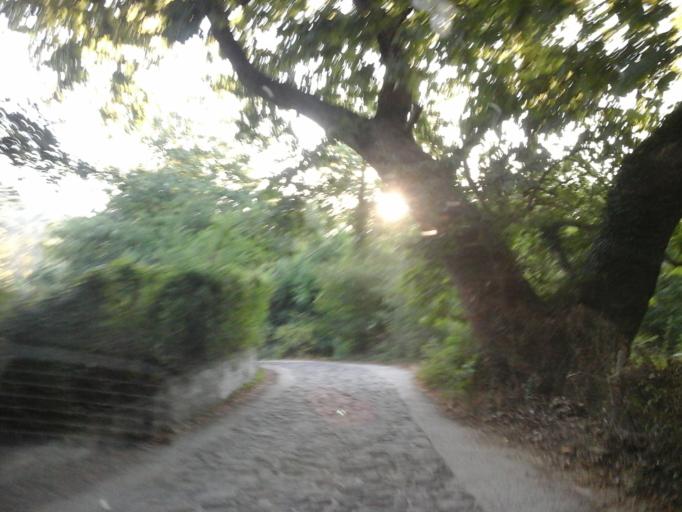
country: GR
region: East Macedonia and Thrace
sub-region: Nomos Evrou
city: Samothraki
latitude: 40.4949
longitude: 25.6092
